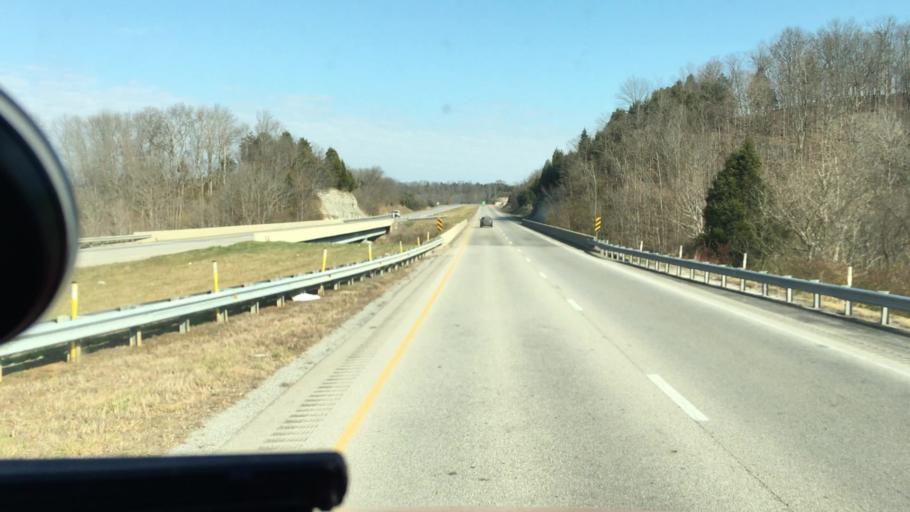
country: US
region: Kentucky
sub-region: Bath County
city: Owingsville
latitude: 38.1175
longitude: -83.7994
